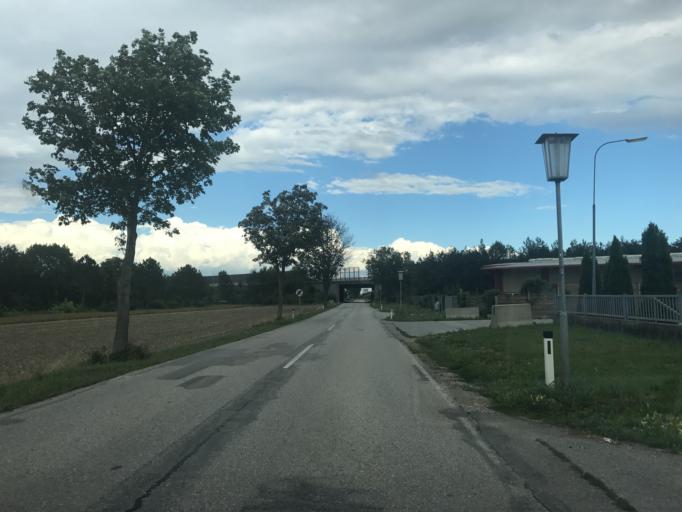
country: AT
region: Lower Austria
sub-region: Politischer Bezirk Wiener Neustadt
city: Theresienfeld
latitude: 47.8637
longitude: 16.1863
